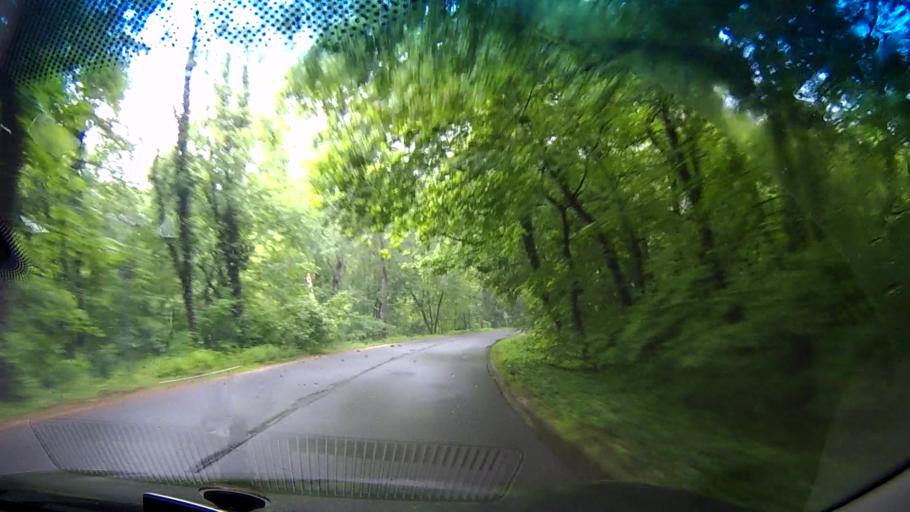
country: HU
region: Komarom-Esztergom
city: Baj
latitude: 47.6183
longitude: 18.3439
